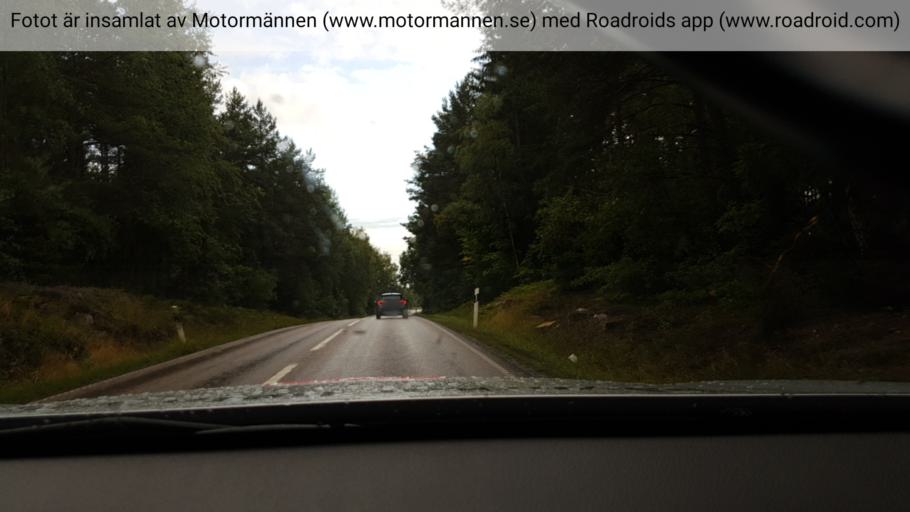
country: SE
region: Stockholm
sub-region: Norrtalje Kommun
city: Norrtalje
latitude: 59.8673
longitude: 18.6943
